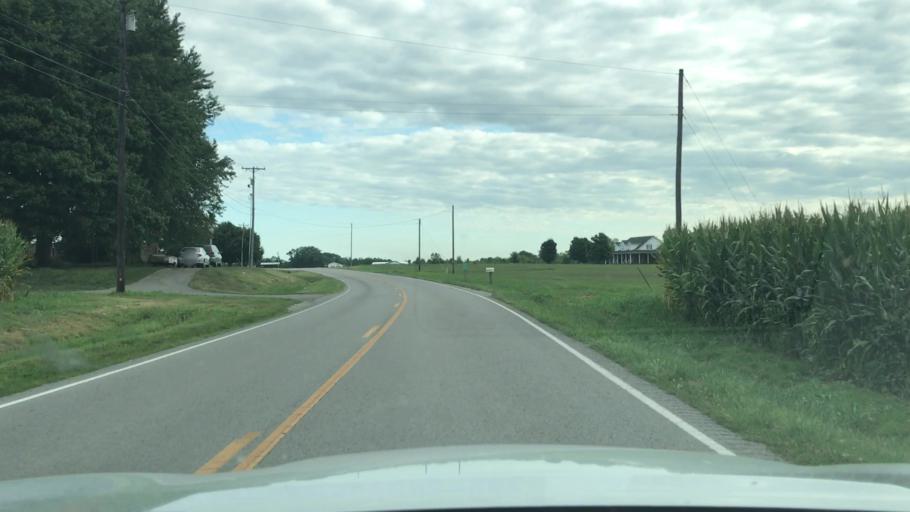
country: US
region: Kentucky
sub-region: Todd County
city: Elkton
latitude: 36.7810
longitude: -87.1636
